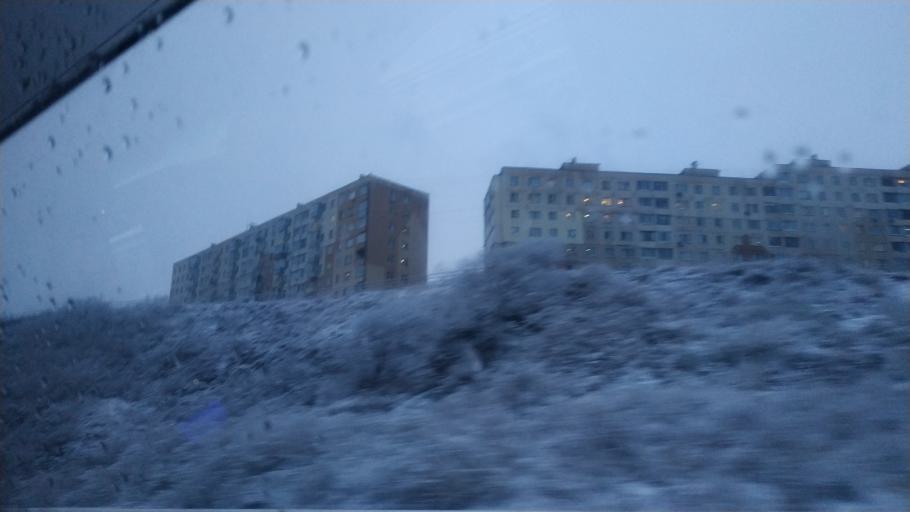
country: RU
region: Primorskiy
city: Vladivostok
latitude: 43.0913
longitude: 131.9800
